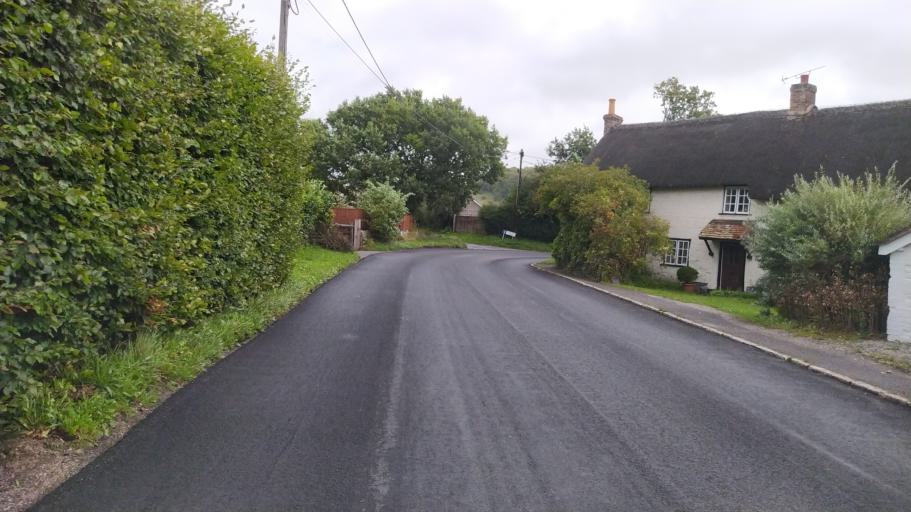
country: GB
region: England
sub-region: Dorset
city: Shaftesbury
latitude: 50.9873
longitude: -2.1637
